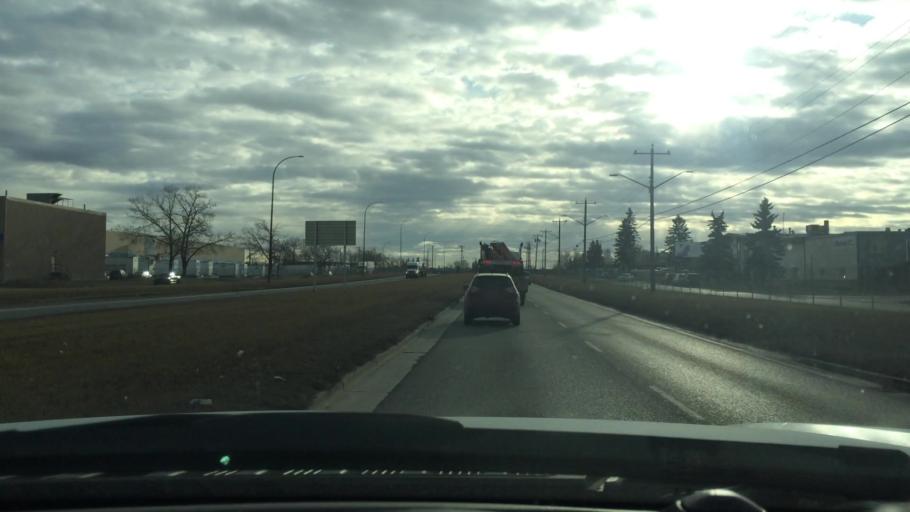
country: CA
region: Alberta
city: Calgary
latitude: 51.0037
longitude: -113.9929
